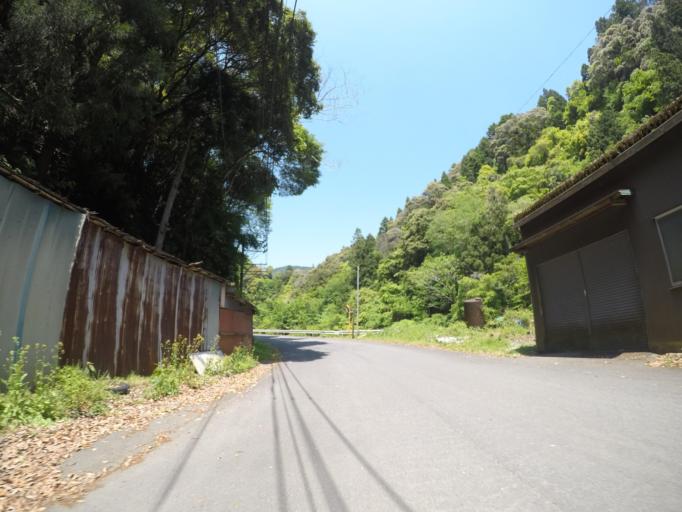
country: JP
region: Shizuoka
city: Shizuoka-shi
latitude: 35.1042
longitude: 138.2280
